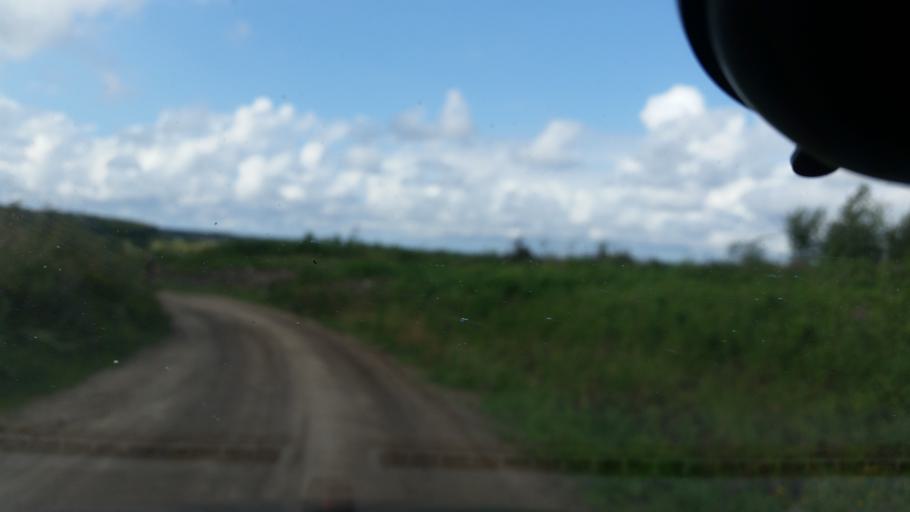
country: PL
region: Pomeranian Voivodeship
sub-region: Powiat wejherowski
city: Choczewo
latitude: 54.7728
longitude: 17.7957
